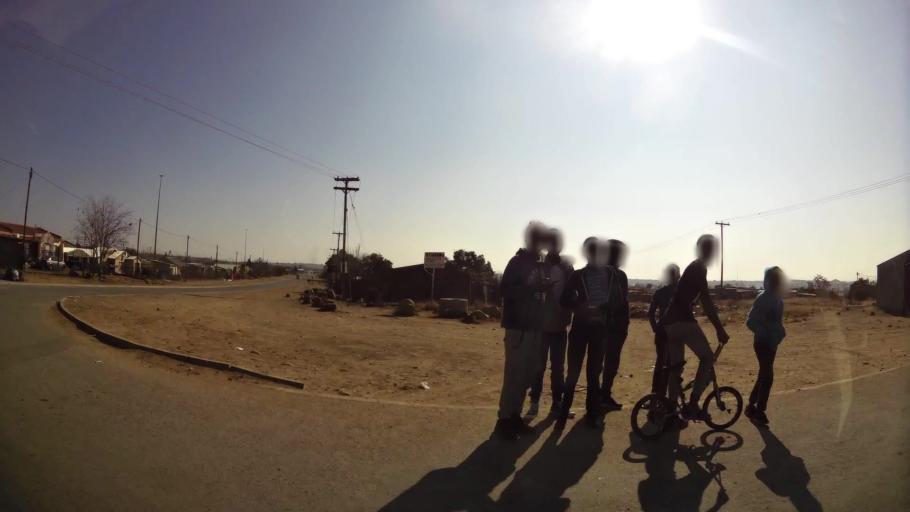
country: ZA
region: Orange Free State
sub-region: Mangaung Metropolitan Municipality
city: Bloemfontein
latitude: -29.2009
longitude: 26.2494
